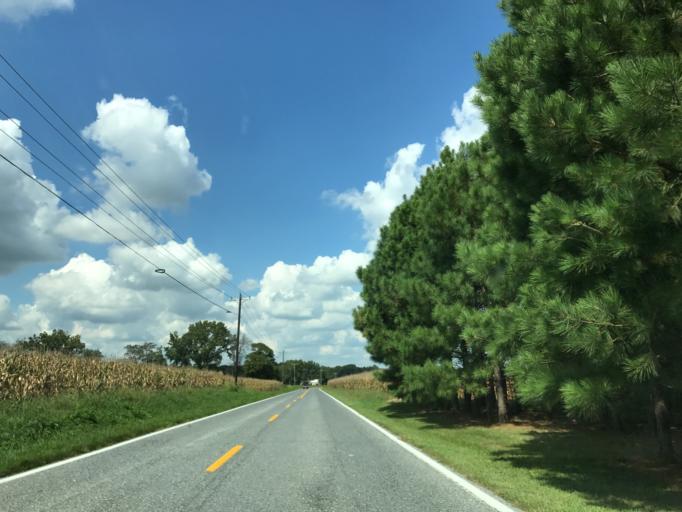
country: US
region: Maryland
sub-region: Caroline County
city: Ridgely
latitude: 39.0649
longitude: -75.9265
